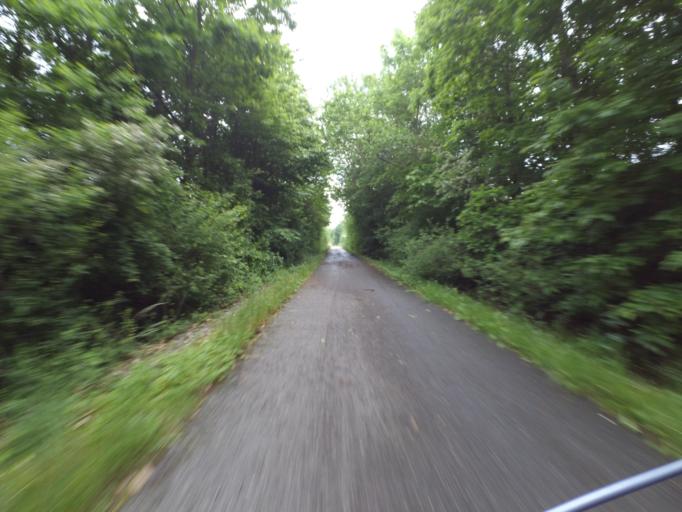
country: DE
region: Rheinland-Pfalz
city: Roth
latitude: 50.0725
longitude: 7.4609
